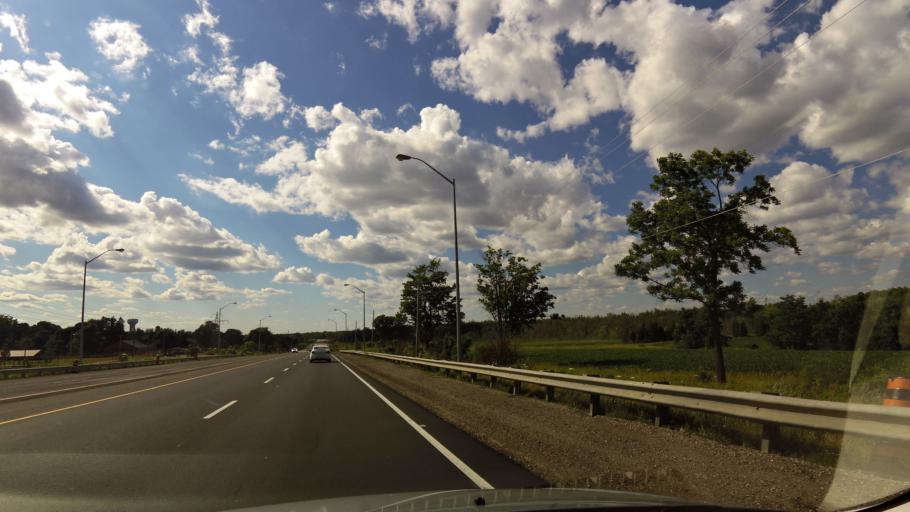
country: CA
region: Ontario
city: Ancaster
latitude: 43.4017
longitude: -80.0380
